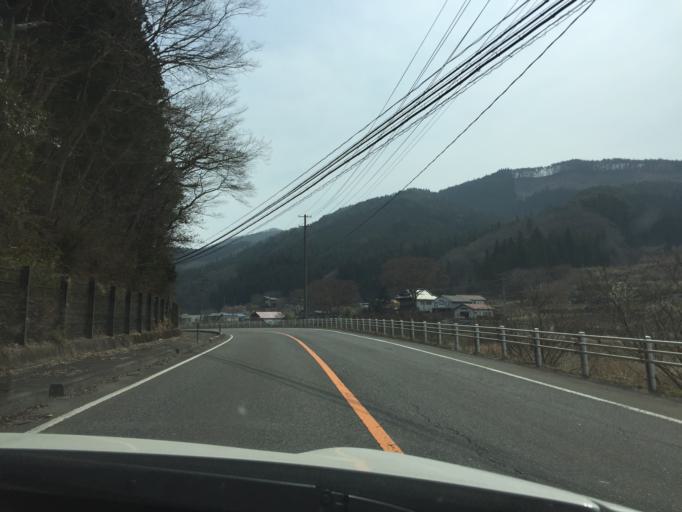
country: JP
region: Fukushima
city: Ishikawa
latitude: 37.0762
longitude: 140.5746
